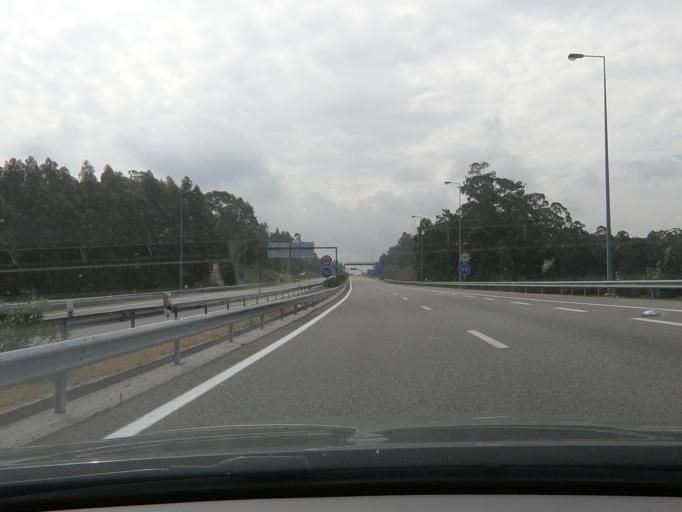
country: PT
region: Aveiro
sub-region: Aveiro
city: Oliveirinha
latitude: 40.6214
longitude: -8.5953
